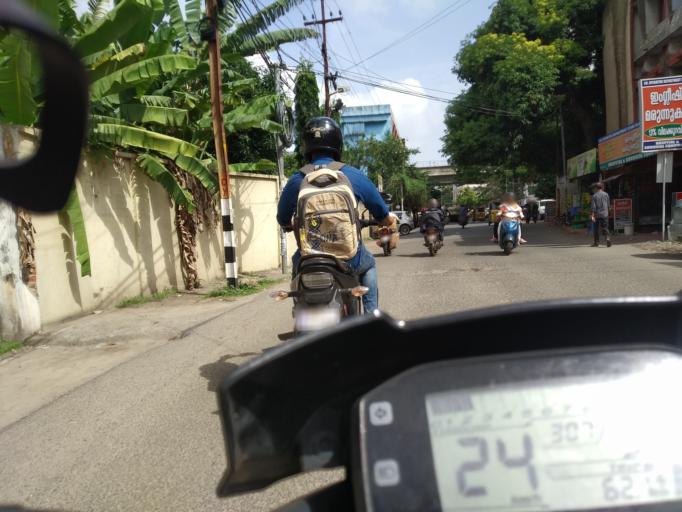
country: IN
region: Kerala
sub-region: Ernakulam
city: Cochin
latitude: 9.9873
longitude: 76.2832
